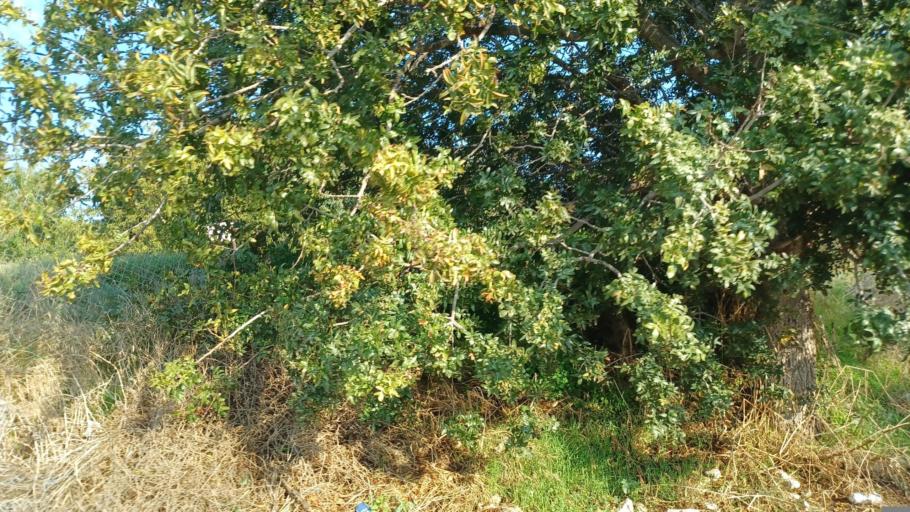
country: CY
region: Pafos
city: Kissonerga
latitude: 34.8241
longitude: 32.3968
